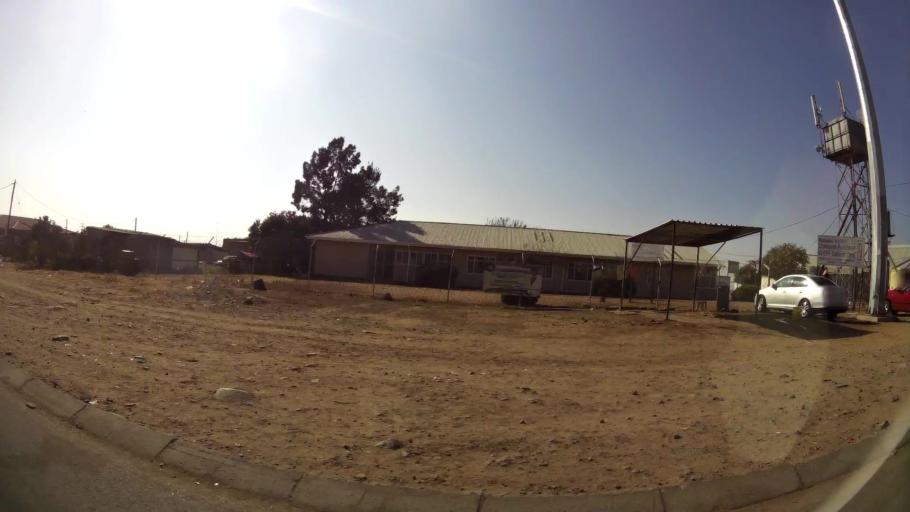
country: ZA
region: Orange Free State
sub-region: Mangaung Metropolitan Municipality
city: Bloemfontein
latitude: -29.1761
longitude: 26.2413
